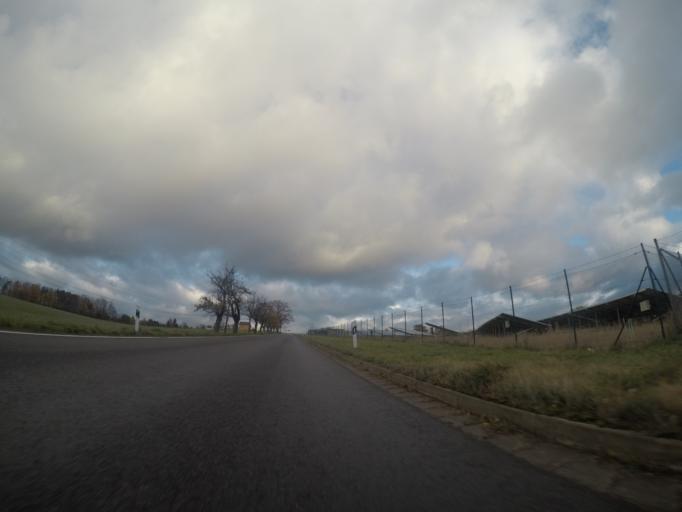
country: DE
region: Thuringia
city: Thonhausen
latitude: 50.8479
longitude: 12.3252
